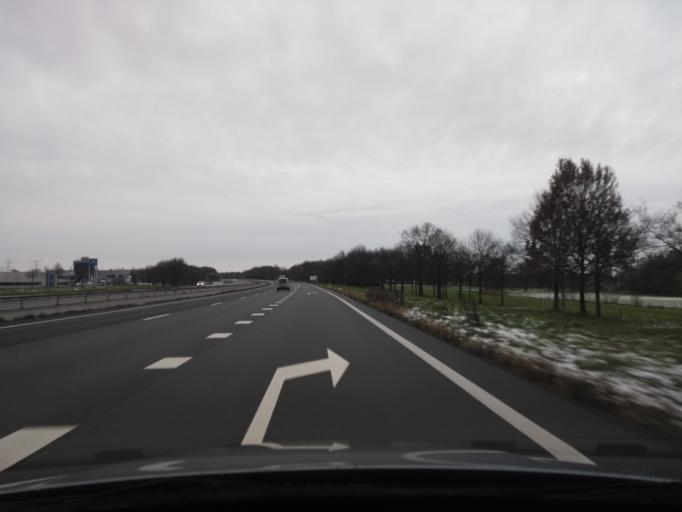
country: NL
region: Overijssel
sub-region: Gemeente Hengelo
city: Hengelo
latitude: 52.2445
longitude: 6.7567
